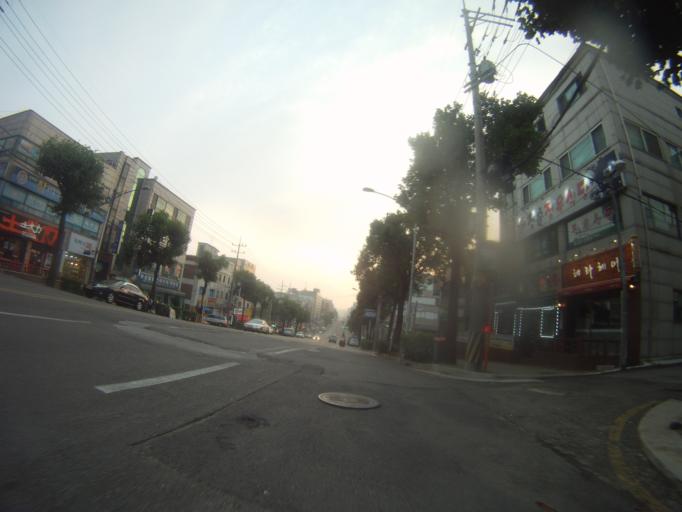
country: KR
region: Incheon
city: Incheon
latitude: 37.4581
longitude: 126.6864
